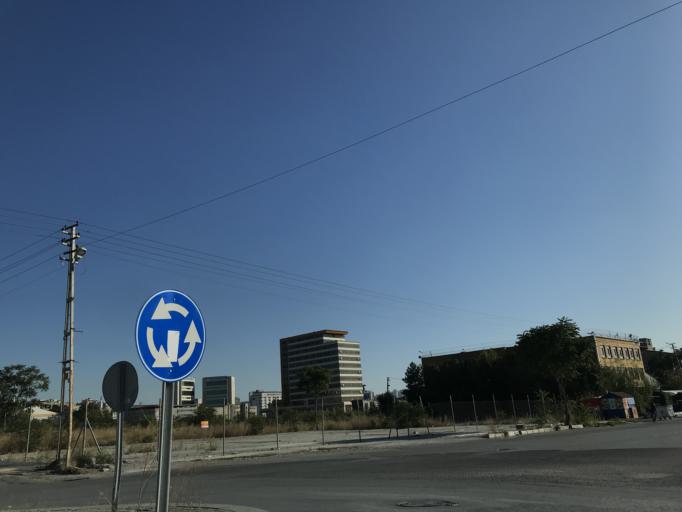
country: TR
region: Ankara
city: Ankara
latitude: 39.9527
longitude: 32.8493
